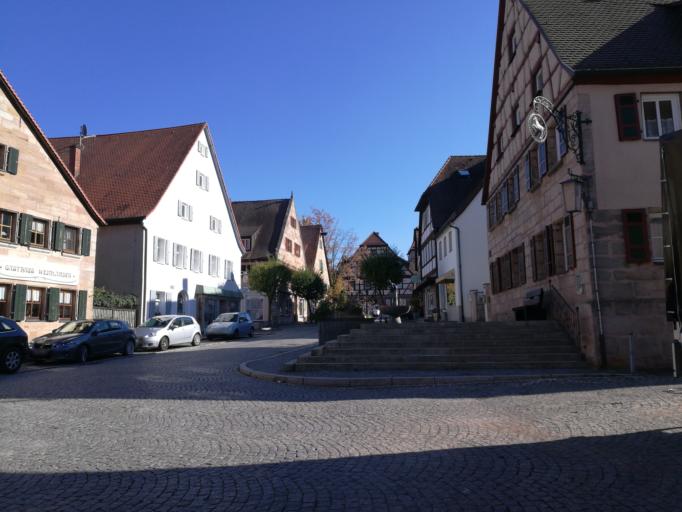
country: DE
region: Bavaria
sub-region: Regierungsbezirk Mittelfranken
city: Cadolzburg
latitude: 49.4584
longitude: 10.8514
